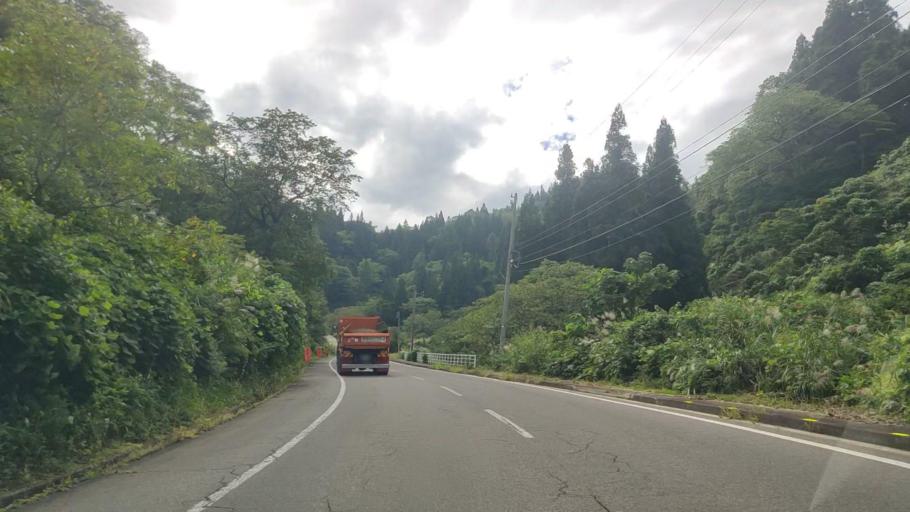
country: JP
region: Nagano
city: Iiyama
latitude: 36.9046
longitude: 138.3142
